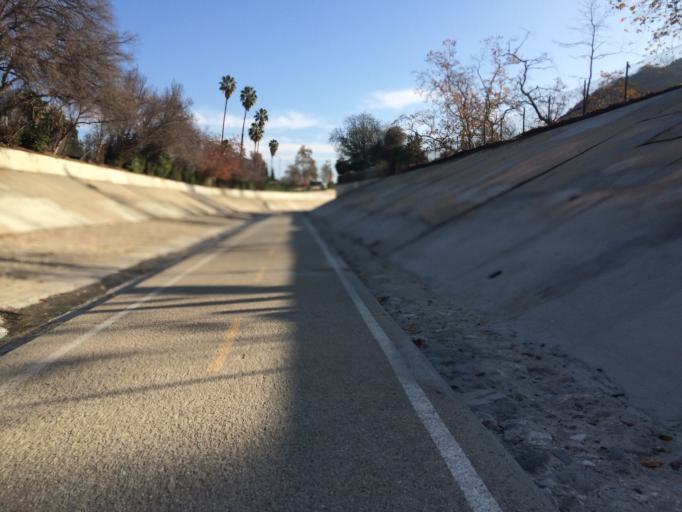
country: US
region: California
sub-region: Los Angeles County
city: South Pasadena
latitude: 34.1020
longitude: -118.1988
